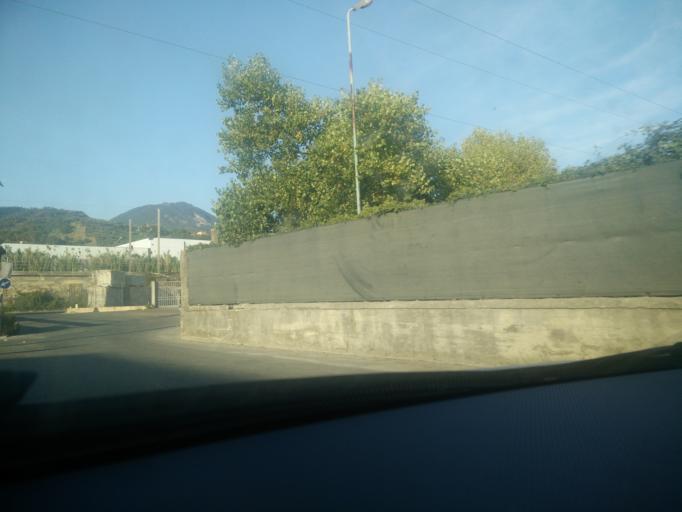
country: IT
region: Tuscany
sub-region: Provincia di Massa-Carrara
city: Carrara
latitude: 44.0407
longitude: 10.0846
